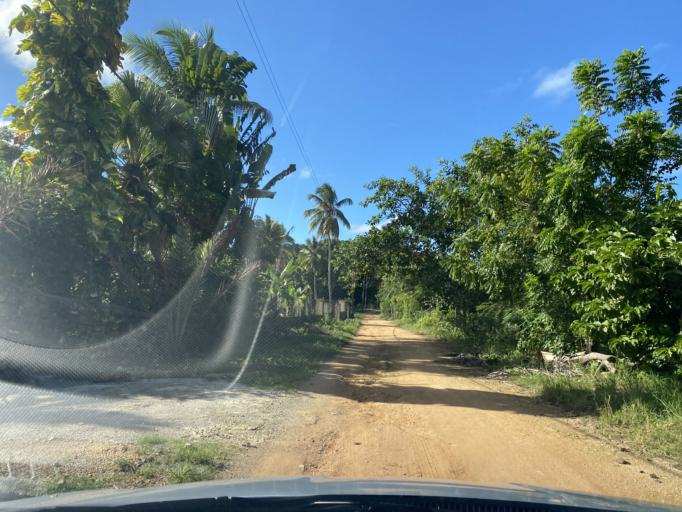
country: DO
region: Samana
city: Las Terrenas
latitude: 19.3081
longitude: -69.5574
